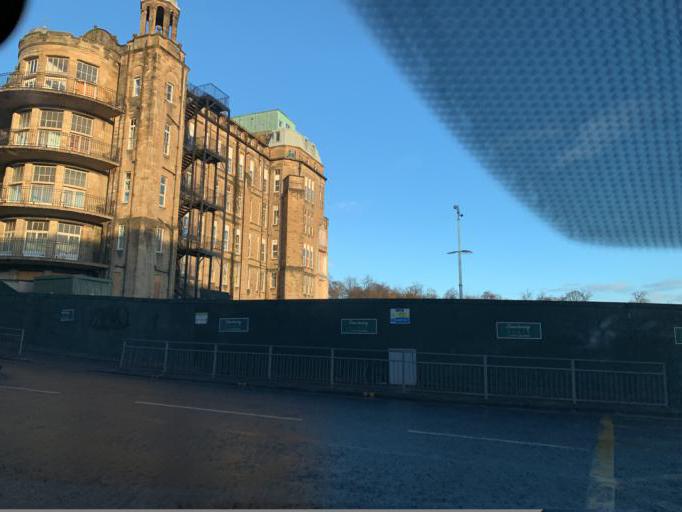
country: GB
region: Scotland
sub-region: East Renfrewshire
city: Giffnock
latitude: 55.8270
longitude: -4.2669
